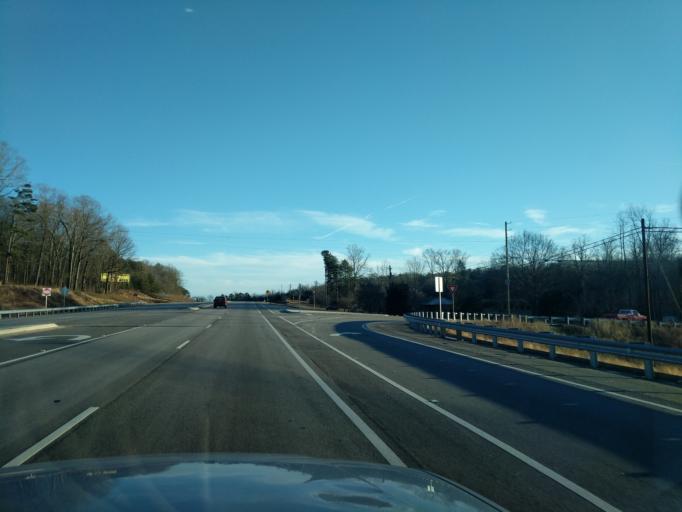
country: US
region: Georgia
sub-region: Stephens County
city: Toccoa
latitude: 34.5299
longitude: -83.2520
